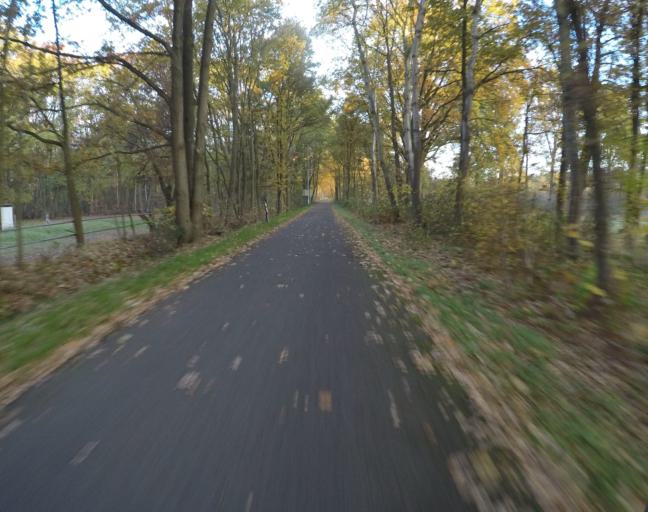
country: BE
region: Flanders
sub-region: Provincie Antwerpen
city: Hulshout
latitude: 51.0754
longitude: 4.8252
